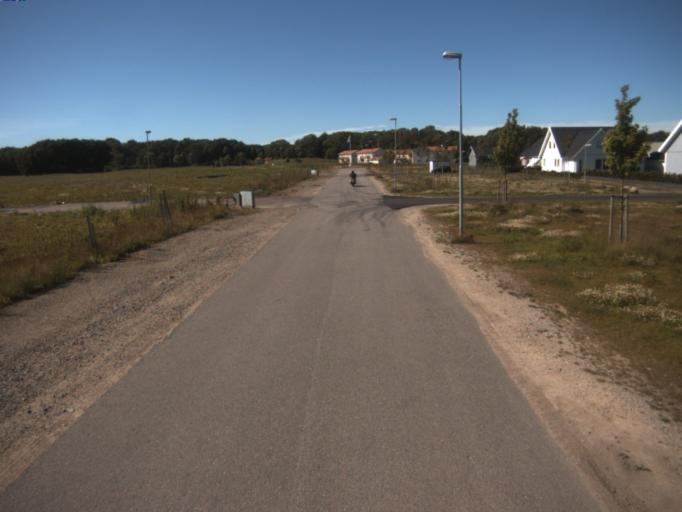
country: SE
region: Skane
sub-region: Helsingborg
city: Odakra
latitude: 56.0961
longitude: 12.7452
